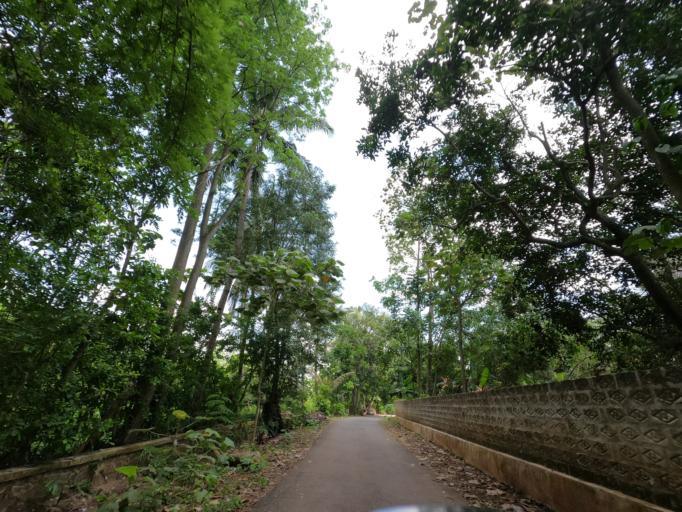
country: ID
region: West Java
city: Pamanukan
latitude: -6.5055
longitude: 107.7720
